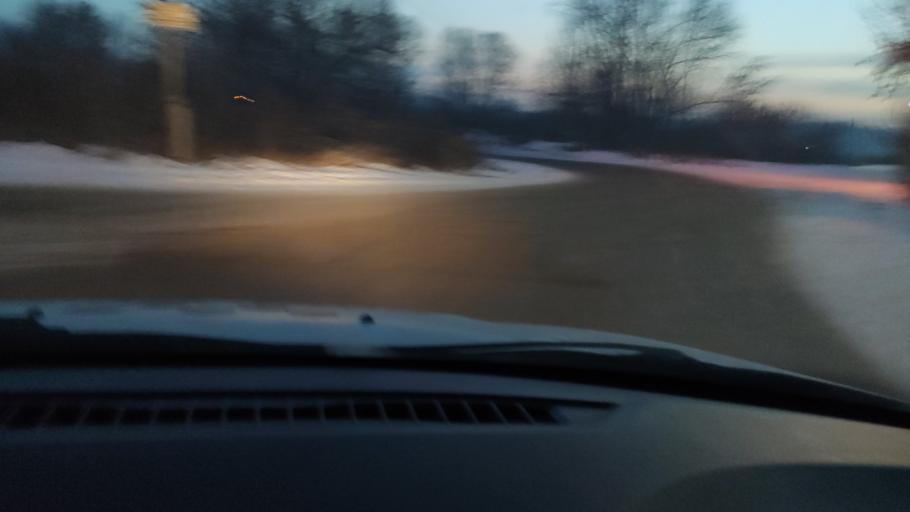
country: RU
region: Perm
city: Kungur
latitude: 57.4344
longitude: 56.9316
